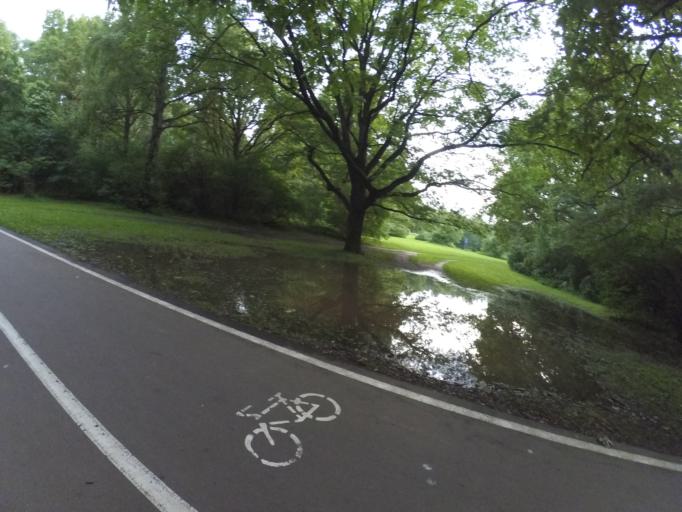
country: RU
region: Moscow
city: Ostankinskiy
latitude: 55.8442
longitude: 37.6094
